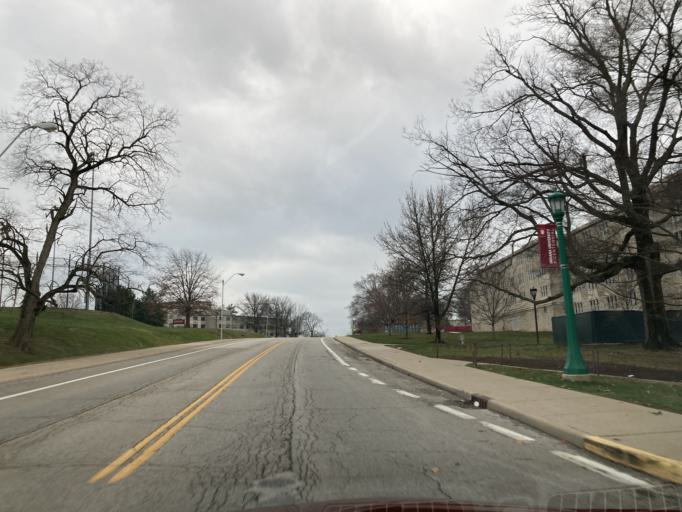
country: US
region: Indiana
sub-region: Monroe County
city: Bloomington
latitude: 39.1778
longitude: -86.5189
